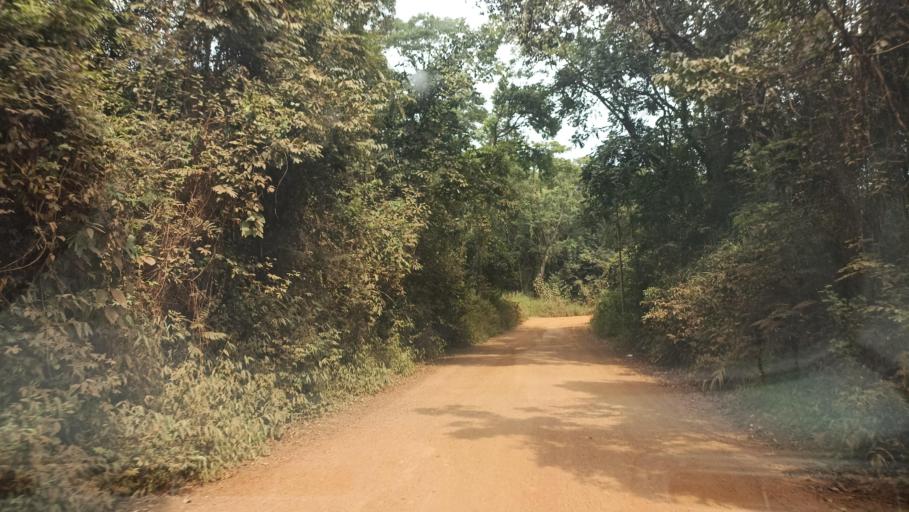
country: BR
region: Minas Gerais
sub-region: Itabirito
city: Itabirito
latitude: -20.3733
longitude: -43.7613
